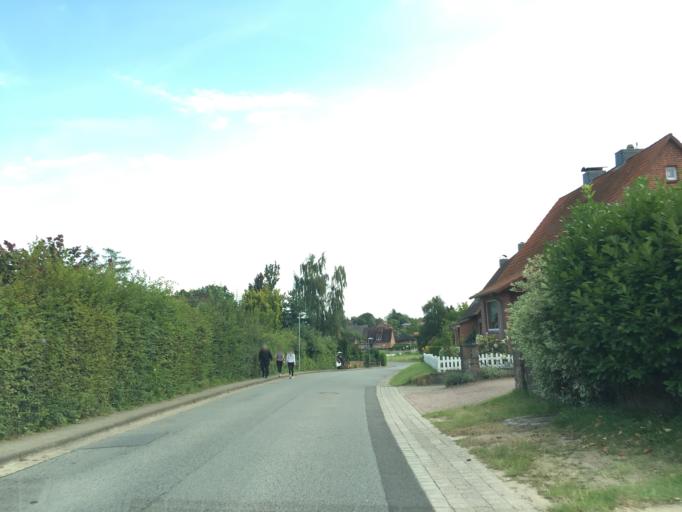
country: DE
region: Lower Saxony
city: Melbeck
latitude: 53.2190
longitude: 10.3875
